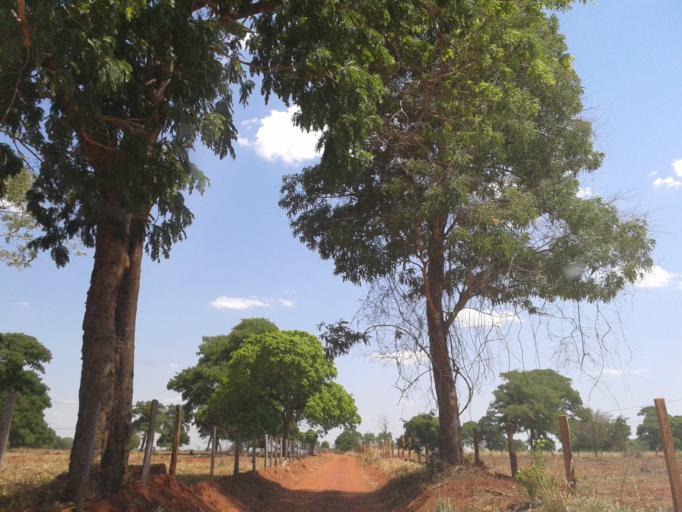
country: BR
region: Minas Gerais
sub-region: Santa Vitoria
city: Santa Vitoria
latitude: -18.8916
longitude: -49.9329
